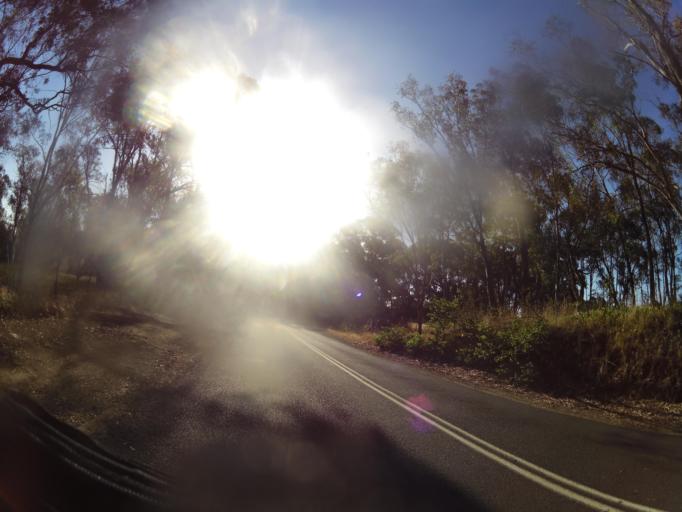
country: AU
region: Victoria
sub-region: Murrindindi
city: Kinglake West
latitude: -37.0201
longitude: 145.1081
